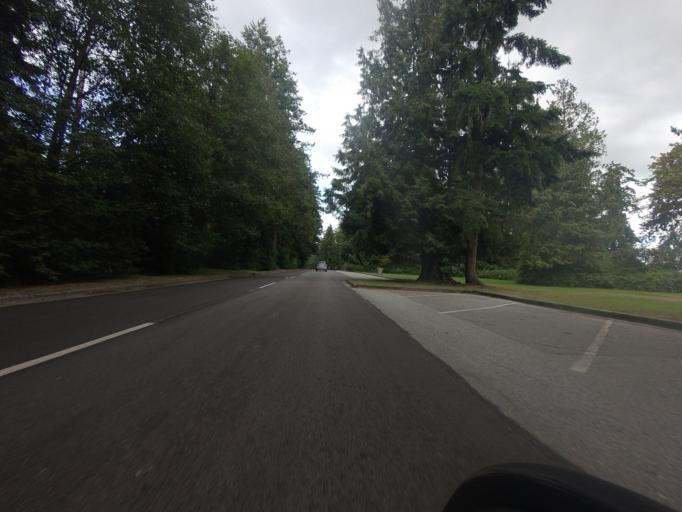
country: CA
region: British Columbia
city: West End
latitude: 49.2972
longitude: -123.1530
